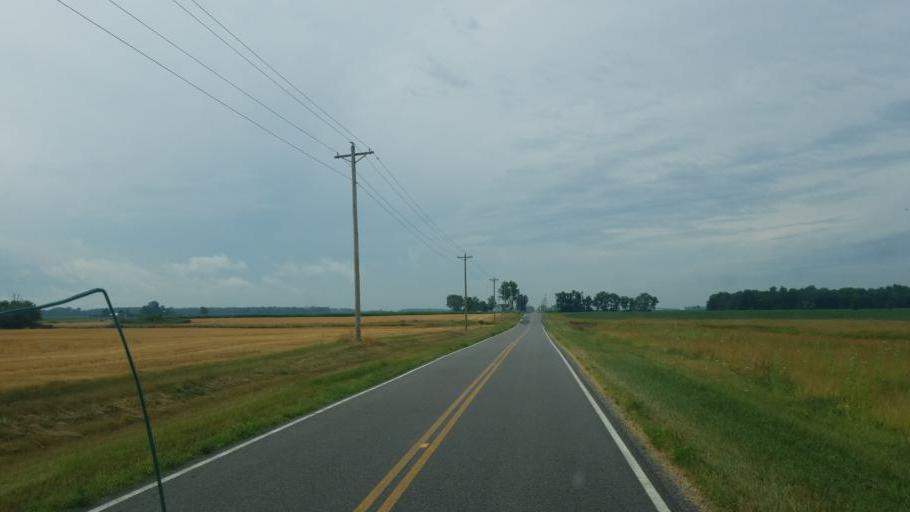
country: US
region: Ohio
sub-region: Defiance County
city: Hicksville
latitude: 41.3353
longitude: -84.6899
